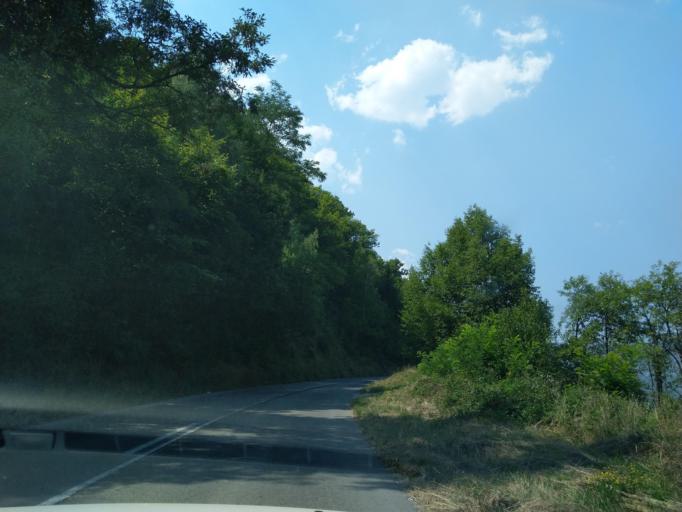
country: RS
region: Central Serbia
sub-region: Zlatiborski Okrug
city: Prijepolje
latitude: 43.3619
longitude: 19.6062
